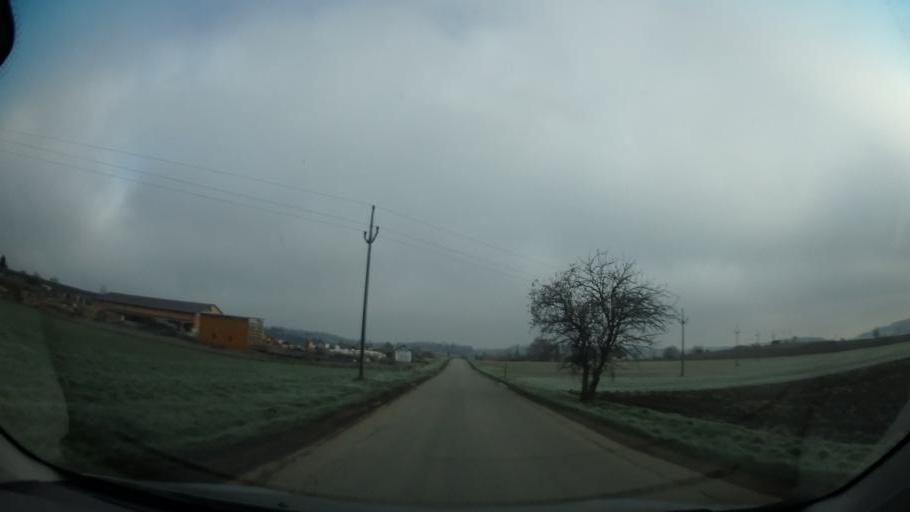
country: CZ
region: Vysocina
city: Mohelno
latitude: 49.1231
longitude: 16.2357
